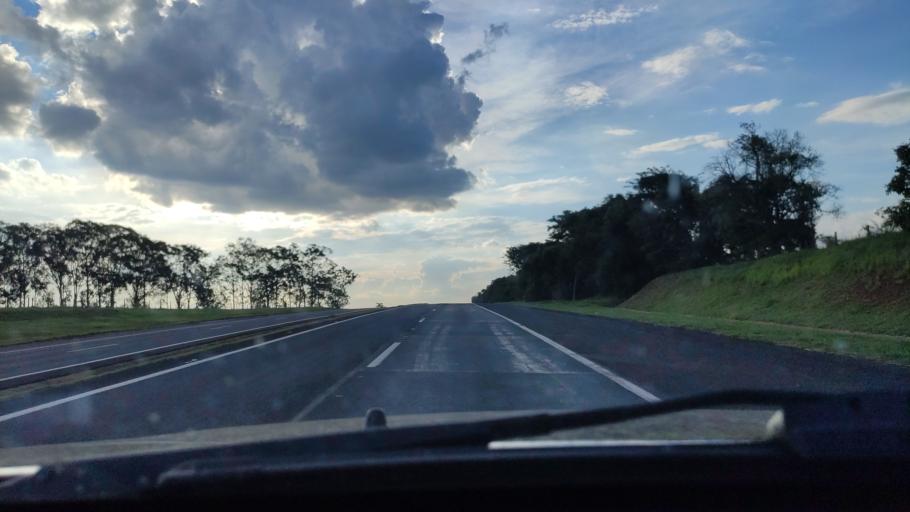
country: BR
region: Sao Paulo
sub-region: Maracai
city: Maracai
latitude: -22.4956
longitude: -50.9046
